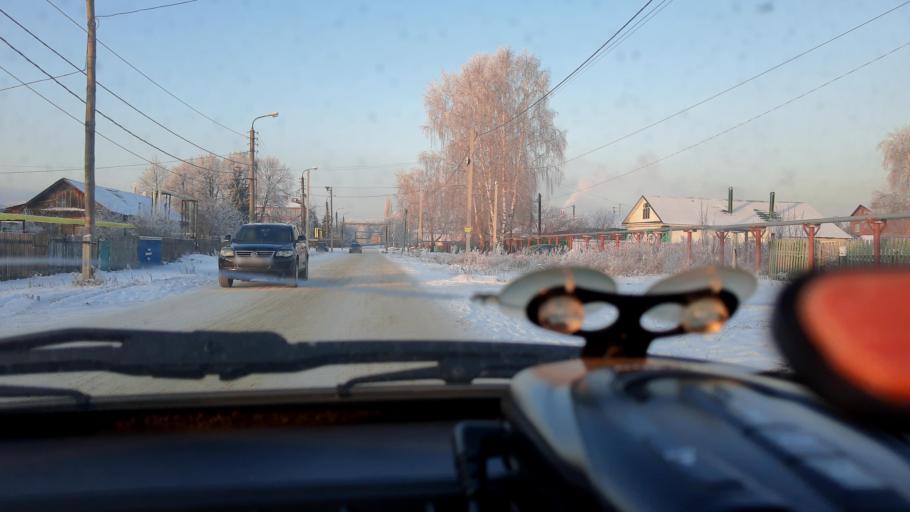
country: RU
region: Bashkortostan
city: Ufa
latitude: 54.6714
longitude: 55.9100
